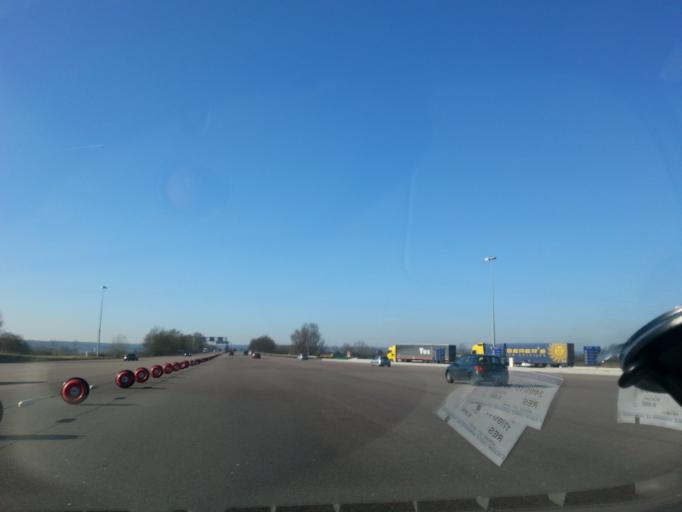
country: FR
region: Ile-de-France
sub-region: Departement des Yvelines
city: Buchelay
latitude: 48.9839
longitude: 1.6804
